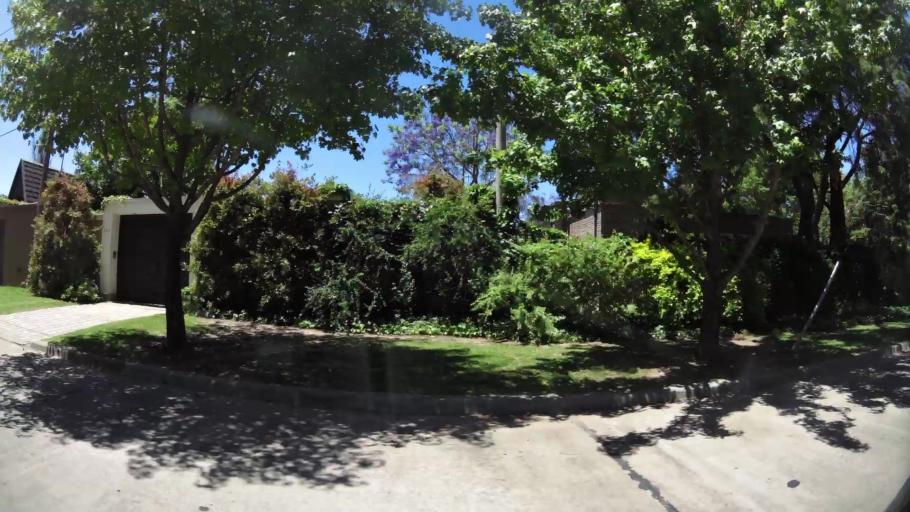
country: AR
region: Santa Fe
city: Rafaela
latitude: -31.2556
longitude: -61.4620
